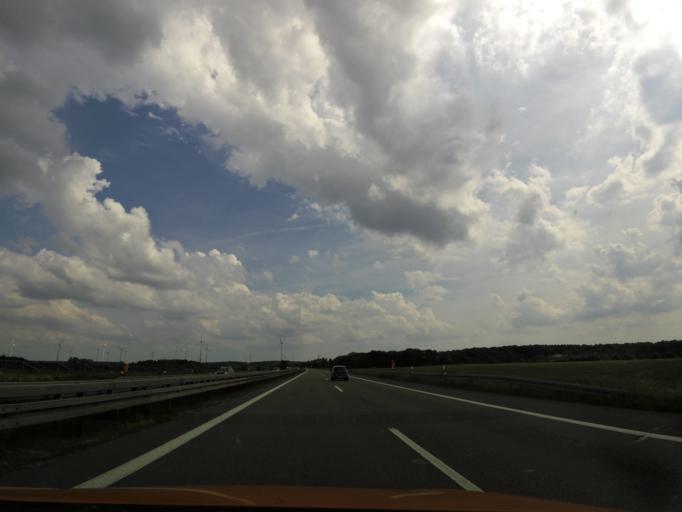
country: DE
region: Brandenburg
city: Gerdshagen
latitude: 53.2450
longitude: 12.1819
